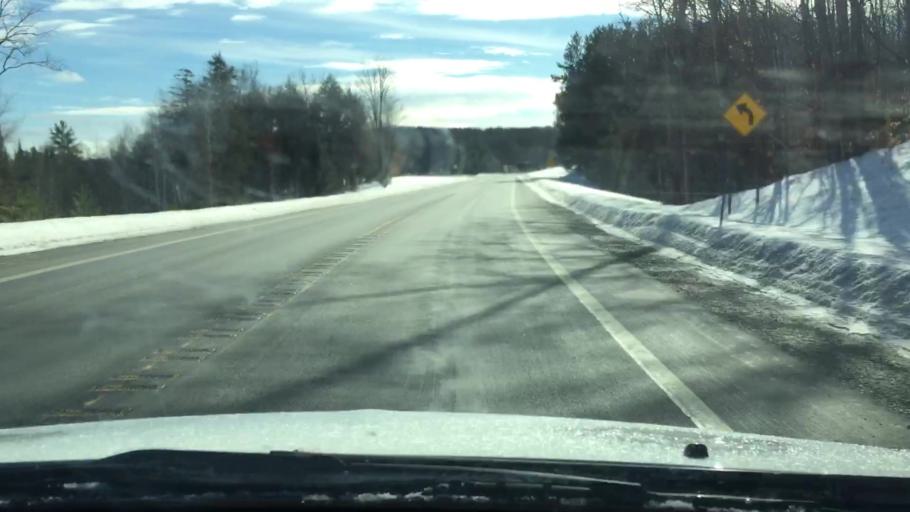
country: US
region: Michigan
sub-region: Antrim County
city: Mancelona
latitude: 44.9959
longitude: -85.0616
